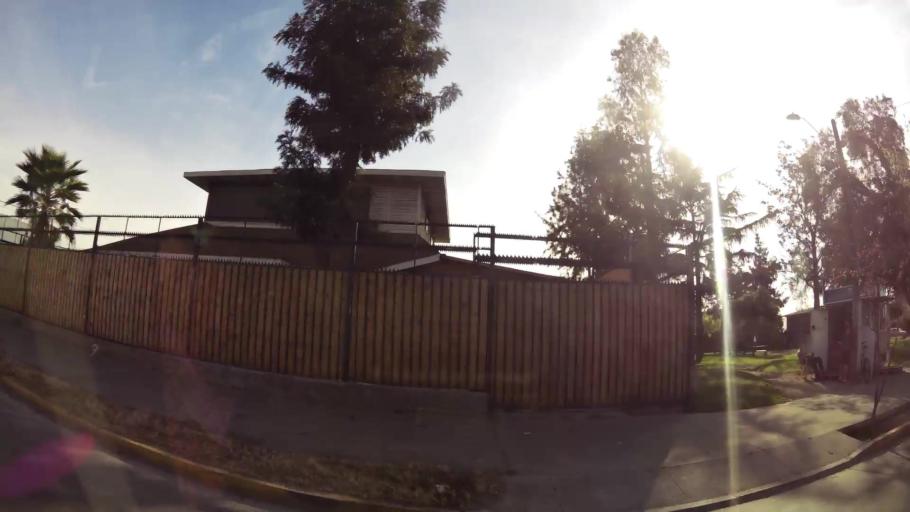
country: CL
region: Santiago Metropolitan
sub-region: Provincia de Santiago
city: Villa Presidente Frei, Nunoa, Santiago, Chile
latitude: -33.5291
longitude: -70.5877
